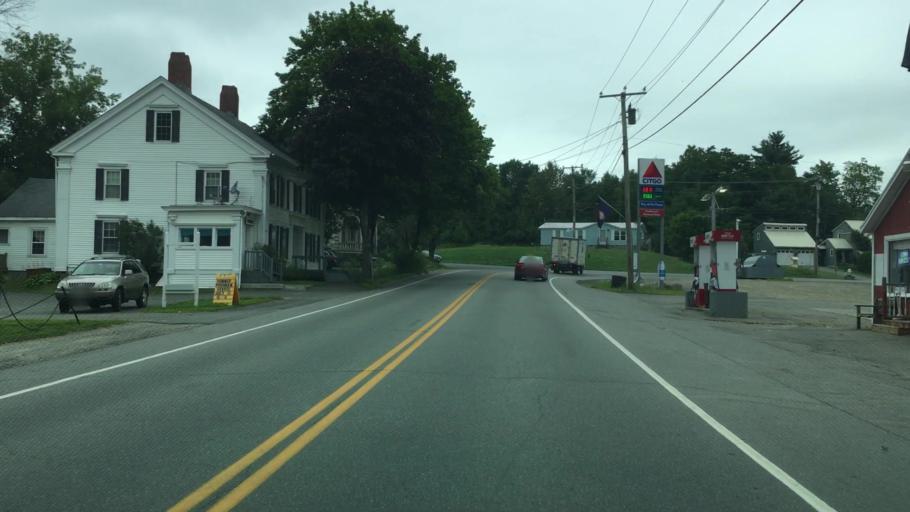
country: US
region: Maine
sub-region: Waldo County
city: Frankfort
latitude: 44.6080
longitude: -68.8742
